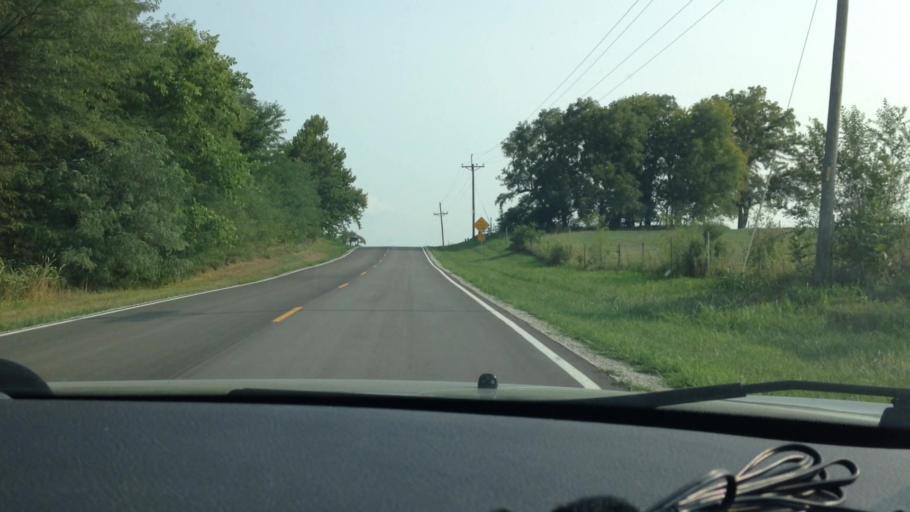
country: US
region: Missouri
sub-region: Platte County
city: Platte City
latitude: 39.4319
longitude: -94.7799
